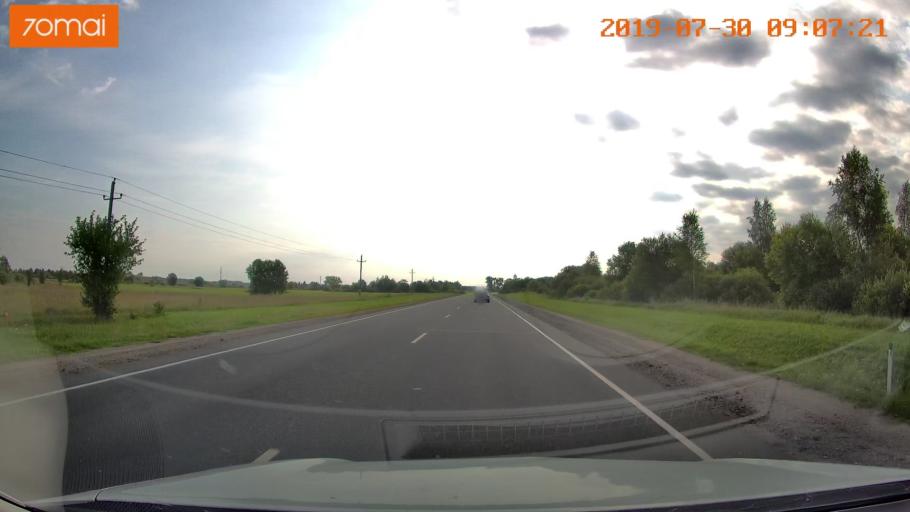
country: RU
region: Kaliningrad
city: Gusev
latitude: 54.6112
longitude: 22.3607
